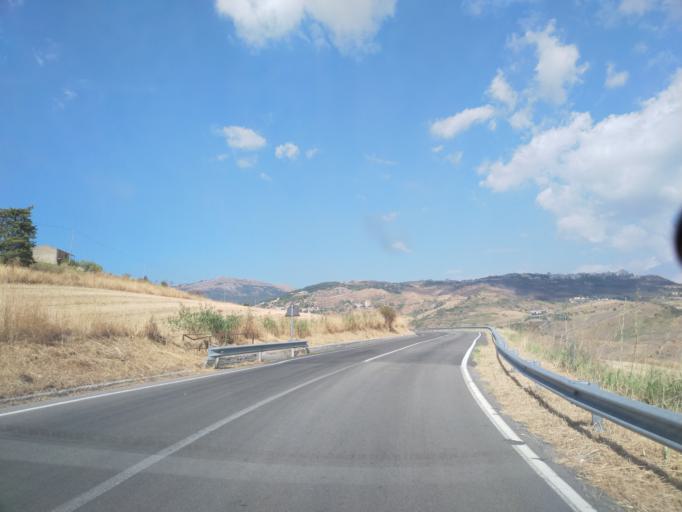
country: IT
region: Sicily
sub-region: Palermo
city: Petralia Sottana
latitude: 37.7897
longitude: 14.0749
